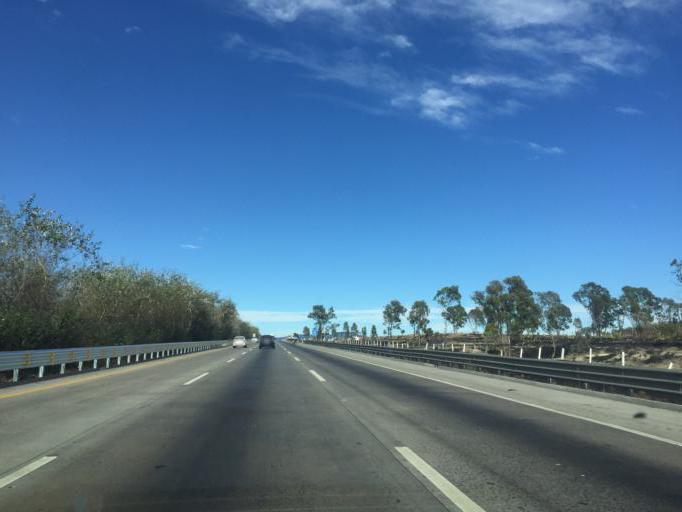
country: MX
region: Mexico
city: San Francisco Soyaniquilpan
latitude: 20.0043
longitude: -99.4994
